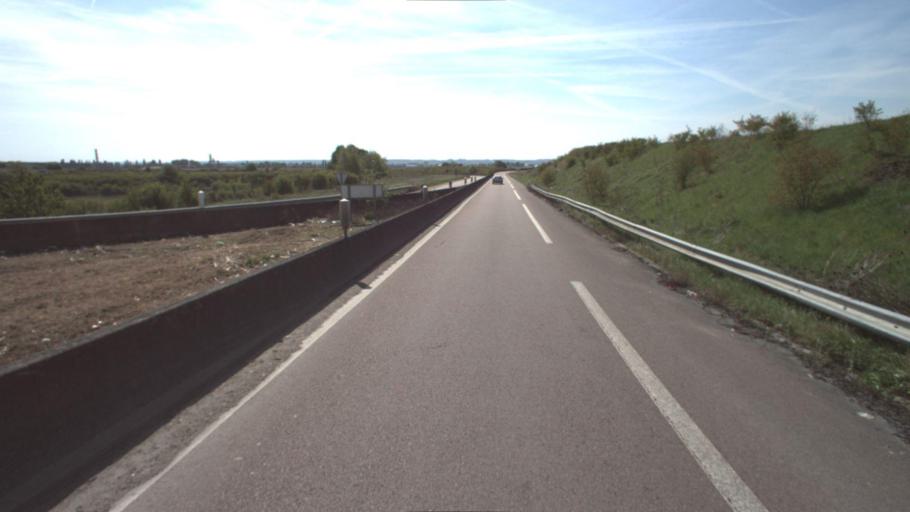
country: FR
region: Ile-de-France
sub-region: Departement de Seine-et-Marne
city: Mitry-Mory
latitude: 49.0012
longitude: 2.6330
